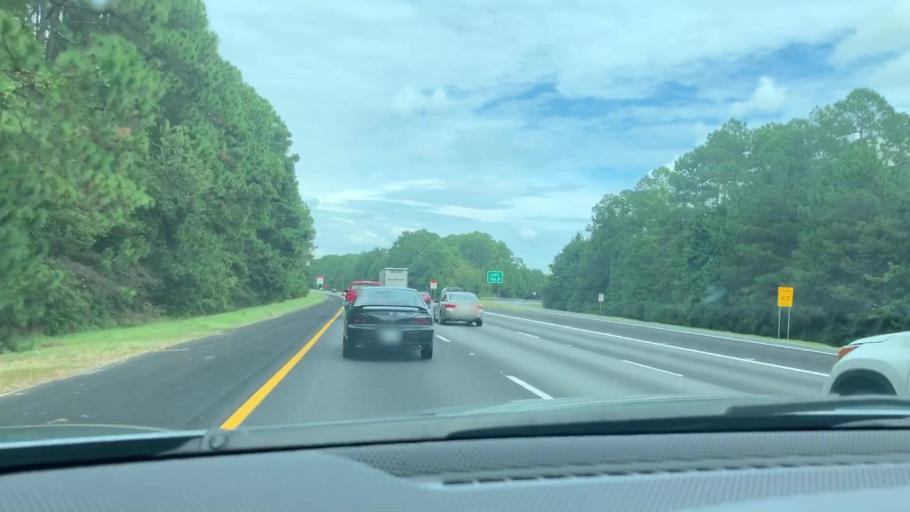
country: US
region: Georgia
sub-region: Chatham County
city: Pooler
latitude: 32.1626
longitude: -81.2209
